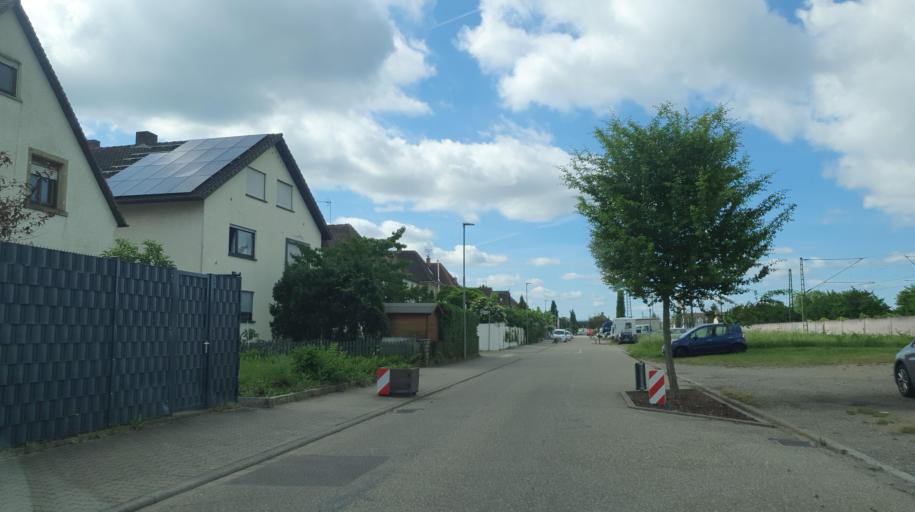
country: DE
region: Baden-Wuerttemberg
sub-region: Karlsruhe Region
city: Weingarten
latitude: 49.0700
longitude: 8.4661
